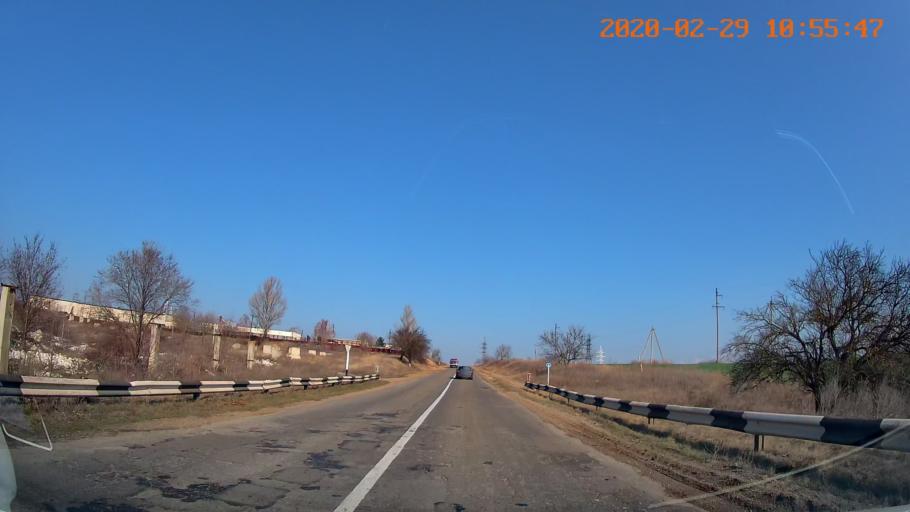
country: MD
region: Telenesti
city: Grigoriopol
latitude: 47.1379
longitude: 29.3255
